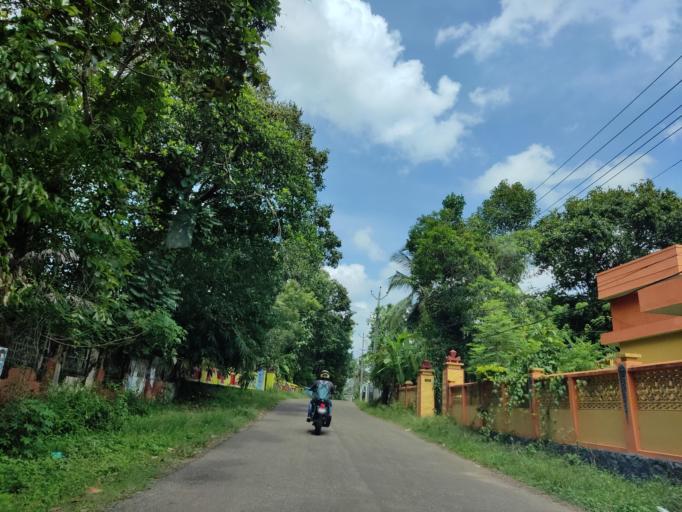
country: IN
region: Kerala
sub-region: Alappuzha
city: Mavelikara
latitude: 9.2530
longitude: 76.5690
